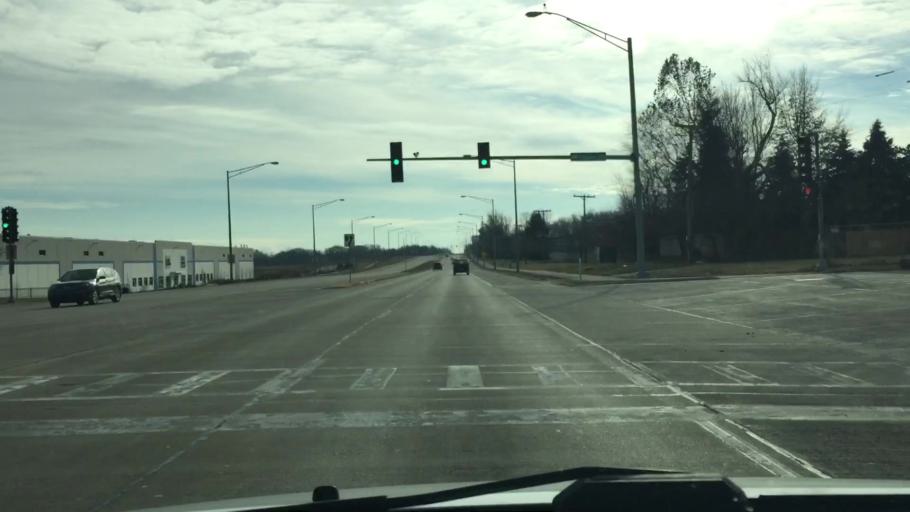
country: US
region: Illinois
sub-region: Kane County
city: Geneva
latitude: 41.9042
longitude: -88.2769
